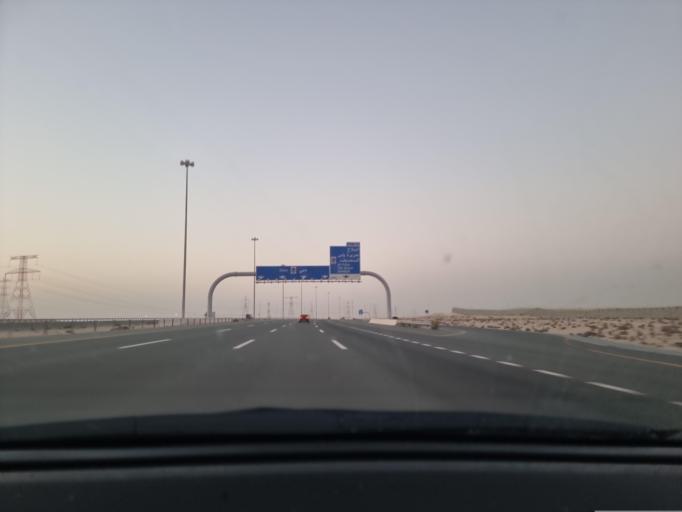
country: AE
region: Abu Dhabi
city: Abu Dhabi
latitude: 24.4516
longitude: 54.7515
